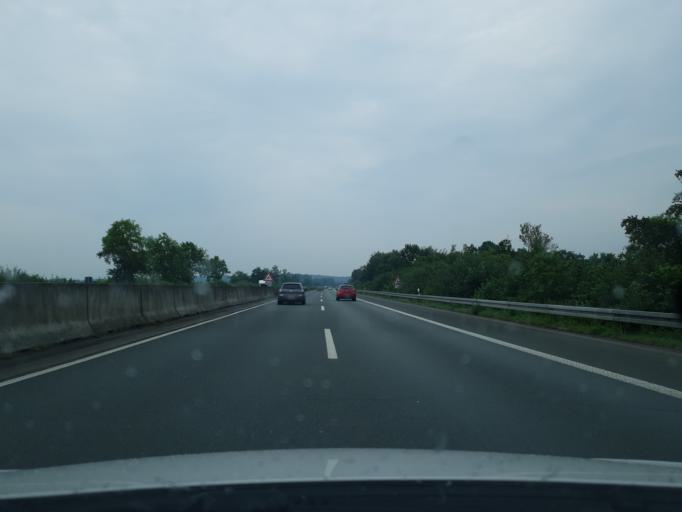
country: DE
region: North Rhine-Westphalia
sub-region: Regierungsbezirk Munster
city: Velen
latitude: 51.8615
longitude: 7.0067
